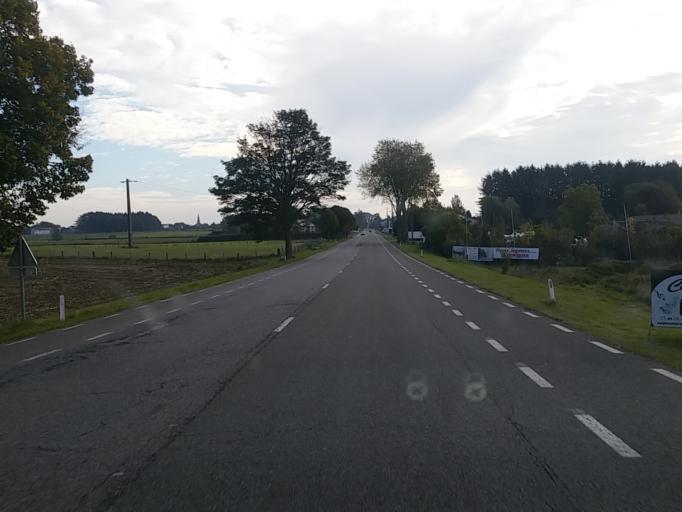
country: BE
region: Wallonia
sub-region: Province du Luxembourg
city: Florenville
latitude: 49.6983
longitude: 5.2889
